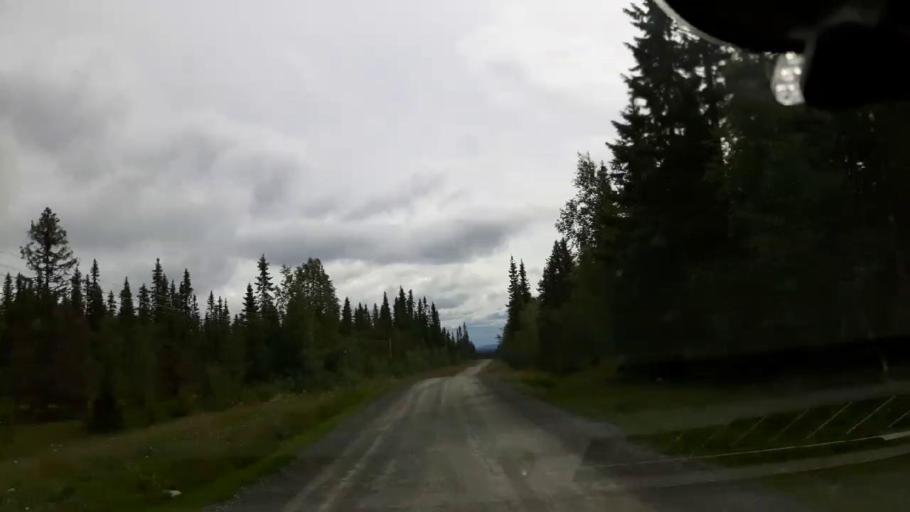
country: SE
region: Jaemtland
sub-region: Krokoms Kommun
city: Valla
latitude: 63.7270
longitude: 13.8421
